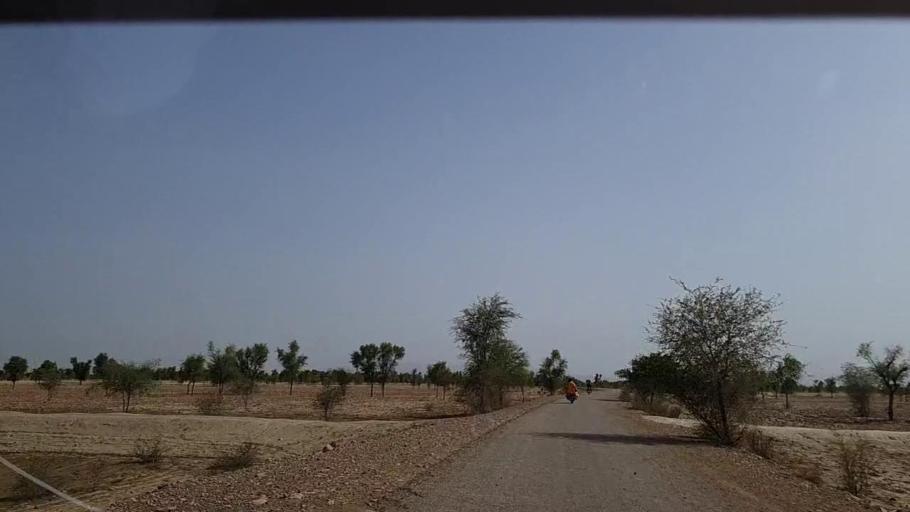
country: PK
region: Sindh
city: Johi
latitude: 26.6191
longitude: 67.4974
